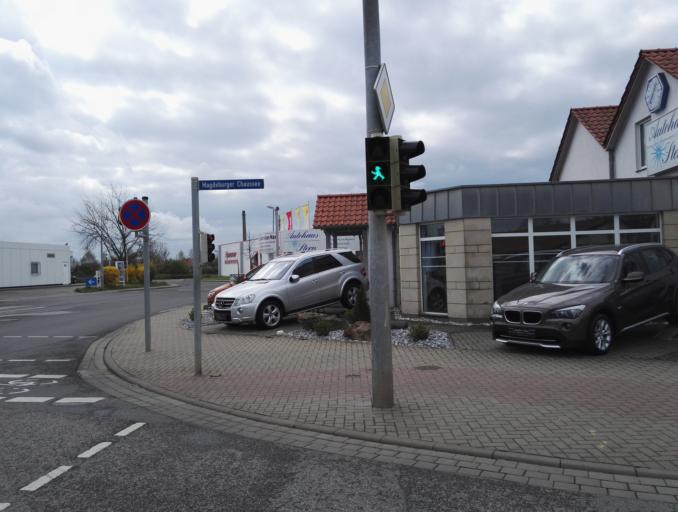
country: DE
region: Saxony-Anhalt
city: Halberstadt
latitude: 51.9013
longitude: 11.0734
